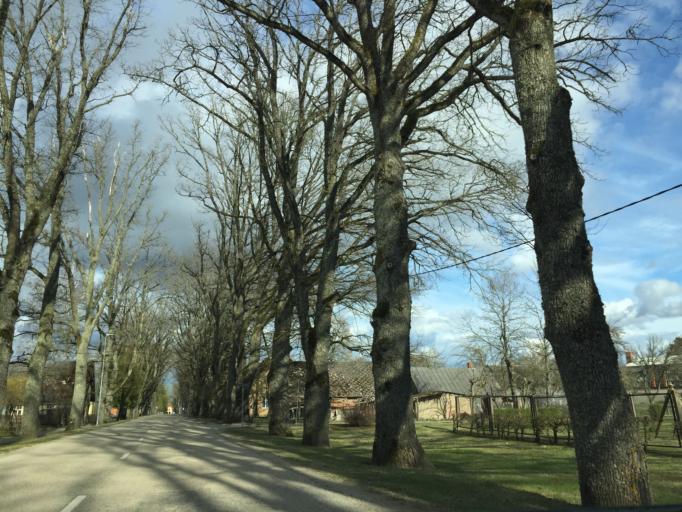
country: LV
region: Burtnieki
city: Matisi
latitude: 57.5973
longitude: 25.0899
